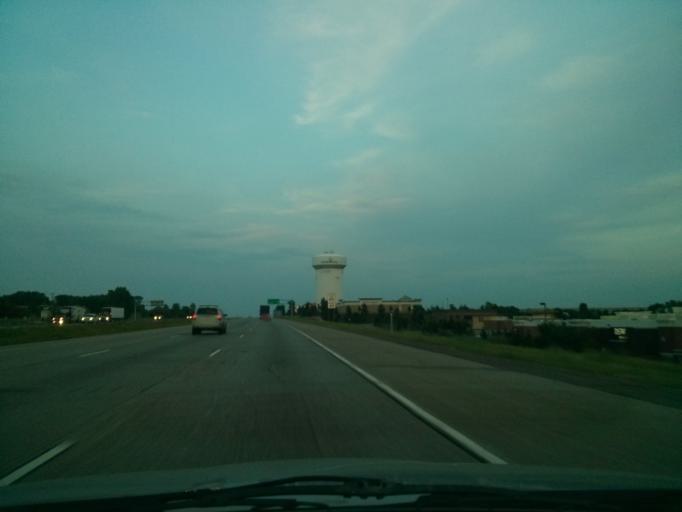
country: US
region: Minnesota
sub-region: Washington County
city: Woodbury
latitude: 44.9484
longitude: -92.9218
